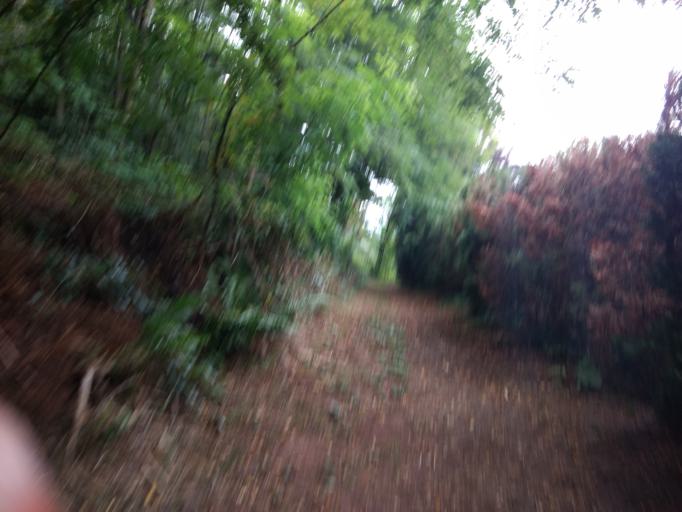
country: DE
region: Saarland
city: Nalbach
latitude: 49.3916
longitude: 6.8021
